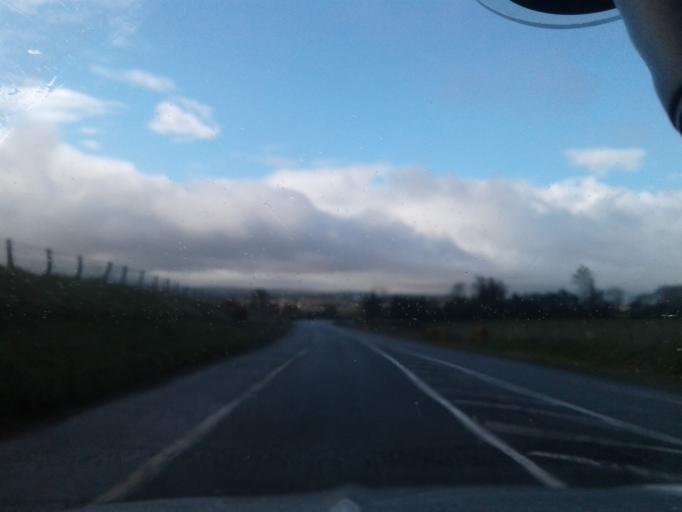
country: IE
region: Ulster
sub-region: County Donegal
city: Ramelton
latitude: 54.9921
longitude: -7.6642
